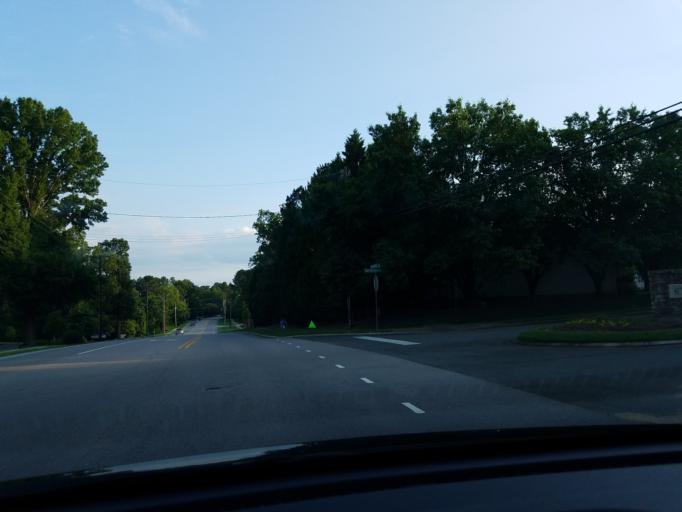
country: US
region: North Carolina
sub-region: Durham County
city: Durham
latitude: 35.9300
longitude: -78.9526
